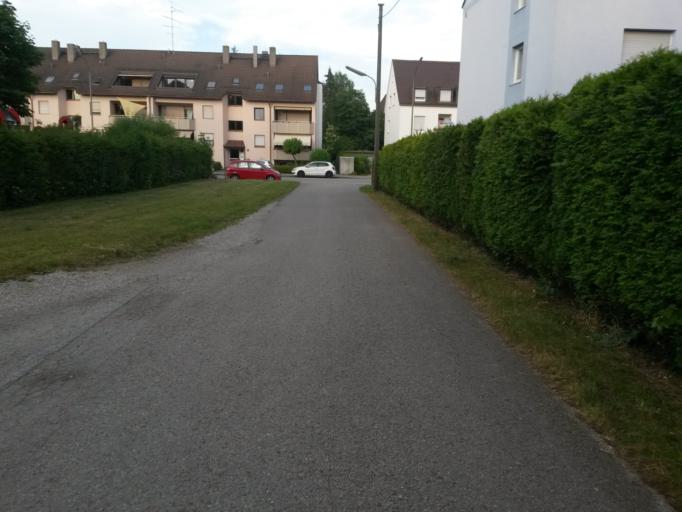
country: DE
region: Bavaria
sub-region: Upper Bavaria
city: Bogenhausen
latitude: 48.1123
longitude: 11.6219
